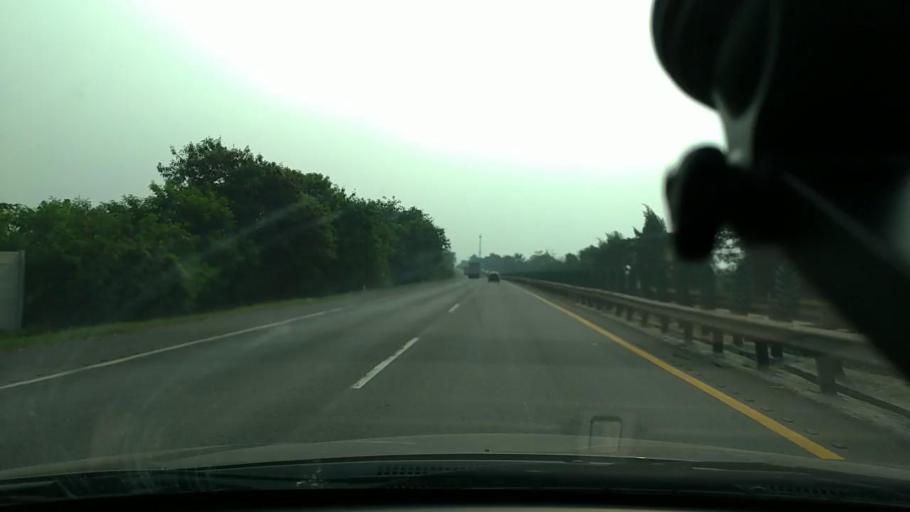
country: ID
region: Banten
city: Serang
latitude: -6.0948
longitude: 106.1631
